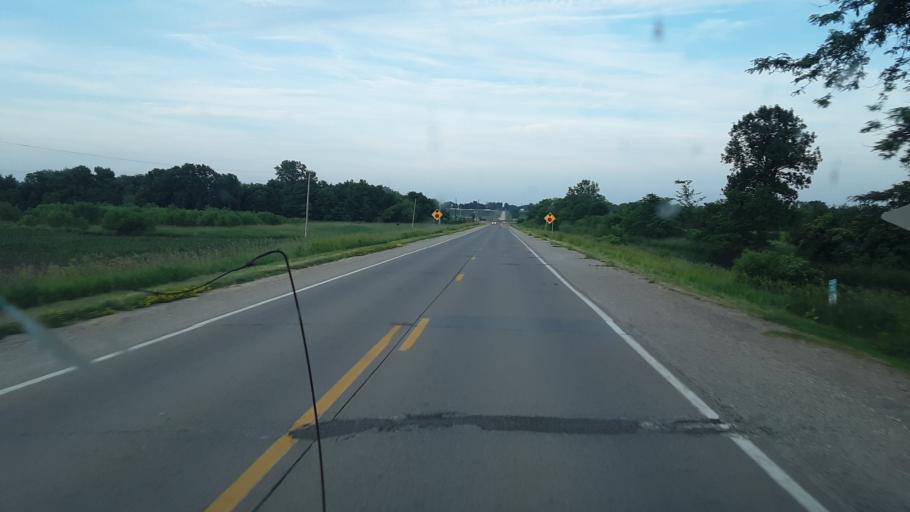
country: US
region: Iowa
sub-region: Benton County
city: Belle Plaine
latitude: 41.9063
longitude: -92.3027
